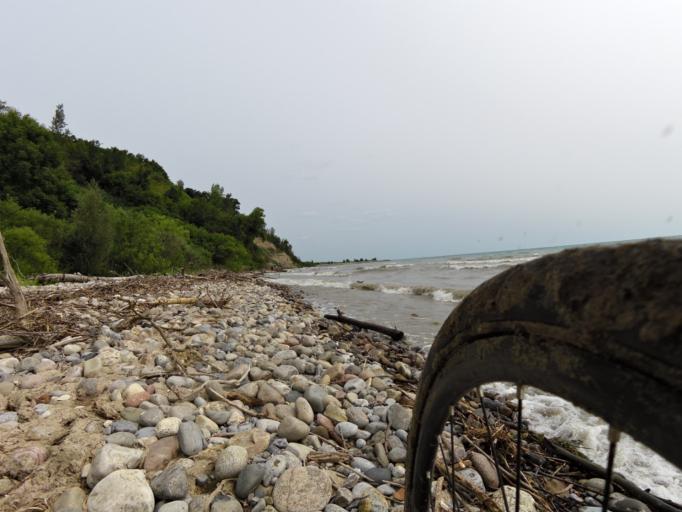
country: CA
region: Ontario
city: Scarborough
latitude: 43.7194
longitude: -79.2224
